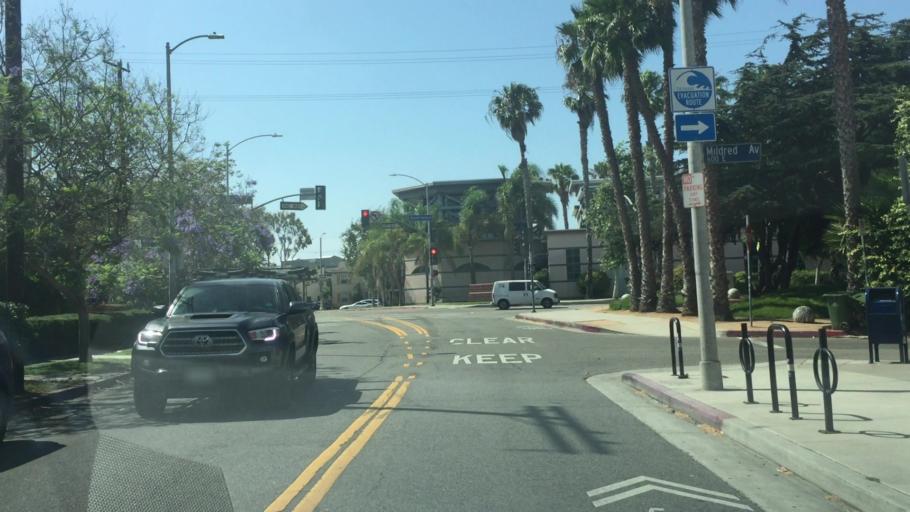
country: US
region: California
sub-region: Los Angeles County
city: Marina del Rey
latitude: 33.9869
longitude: -118.4649
